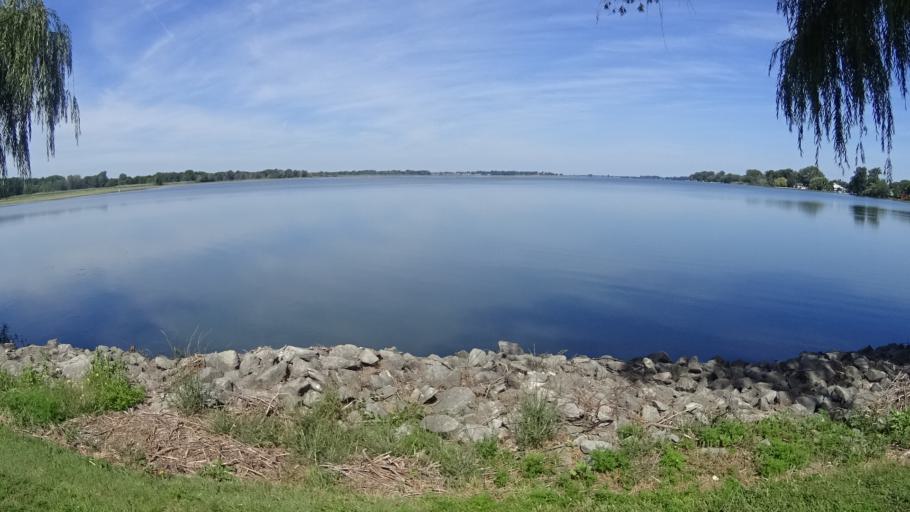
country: US
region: Ohio
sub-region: Erie County
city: Huron
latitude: 41.4308
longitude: -82.6221
